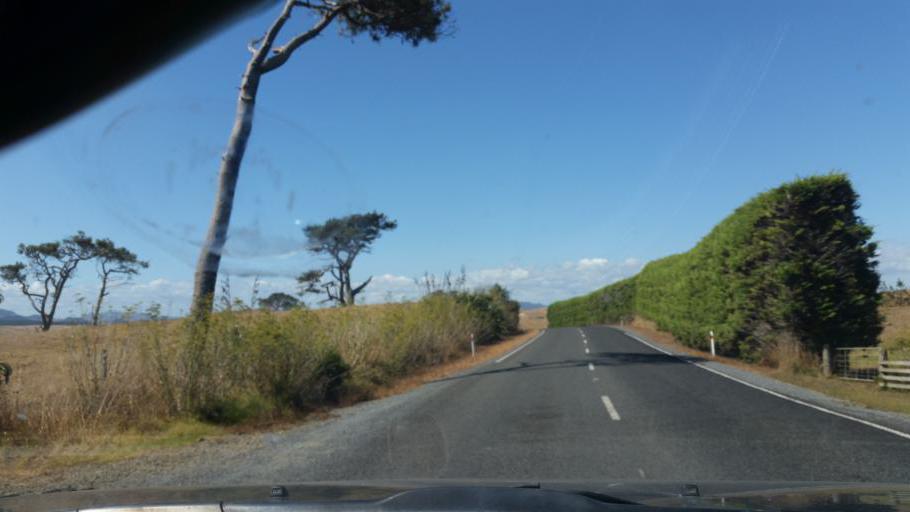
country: NZ
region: Northland
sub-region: Kaipara District
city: Dargaville
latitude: -35.9474
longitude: 173.7700
